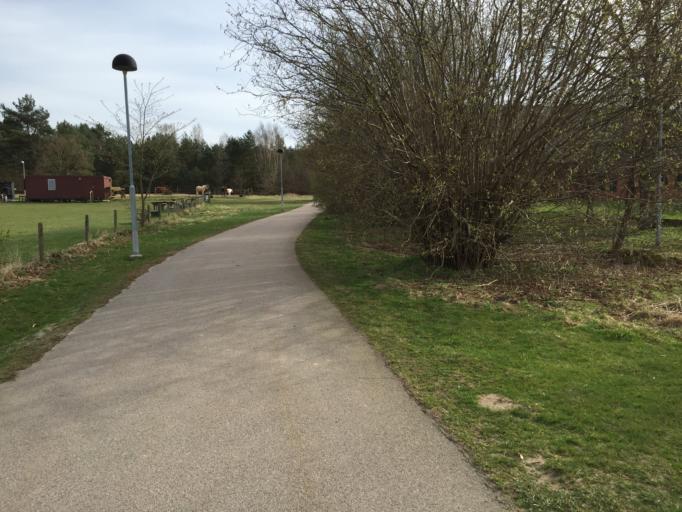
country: SE
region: Skane
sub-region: Lunds Kommun
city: Veberod
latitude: 55.6272
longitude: 13.5033
